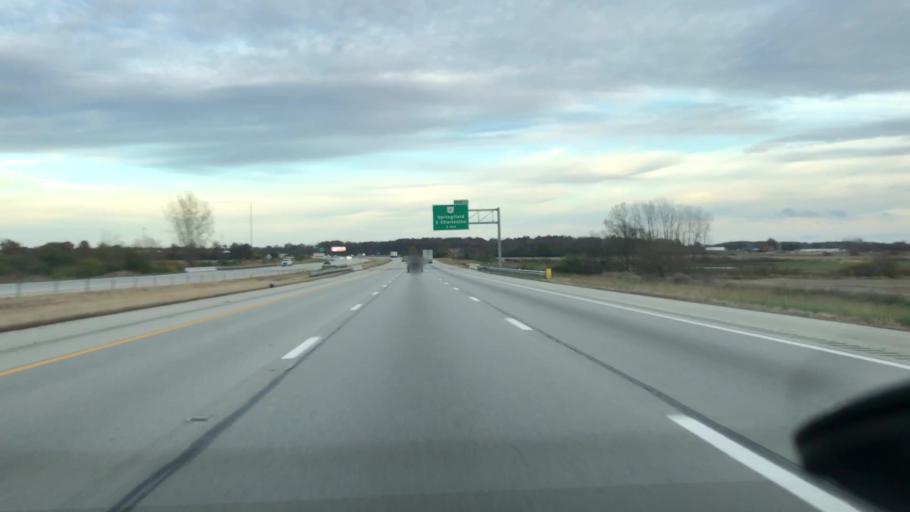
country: US
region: Ohio
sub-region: Clark County
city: Springfield
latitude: 39.8898
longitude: -83.7436
